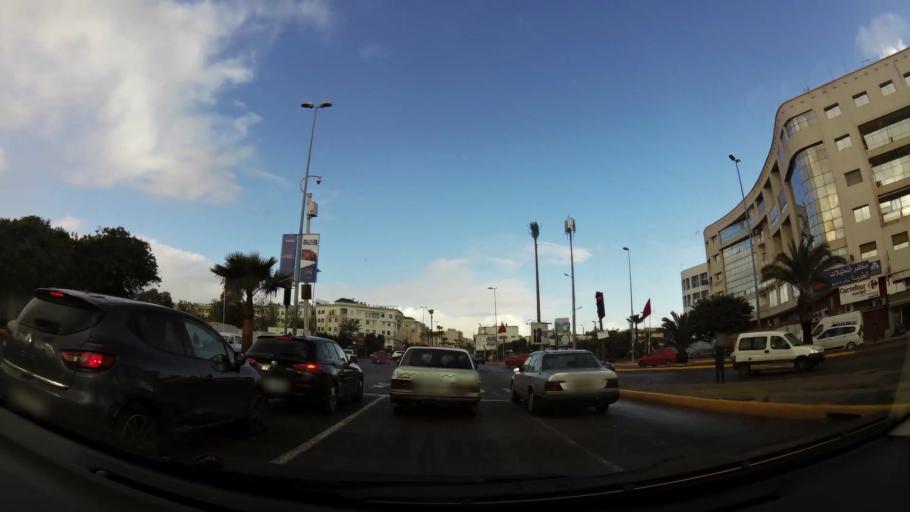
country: MA
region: Grand Casablanca
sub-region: Casablanca
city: Casablanca
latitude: 33.5620
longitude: -7.6684
